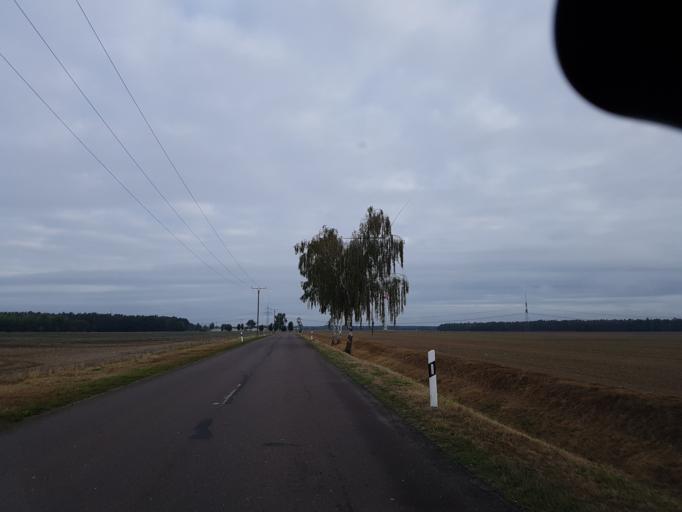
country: DE
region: Saxony-Anhalt
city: Klieken
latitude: 51.9364
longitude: 12.3211
